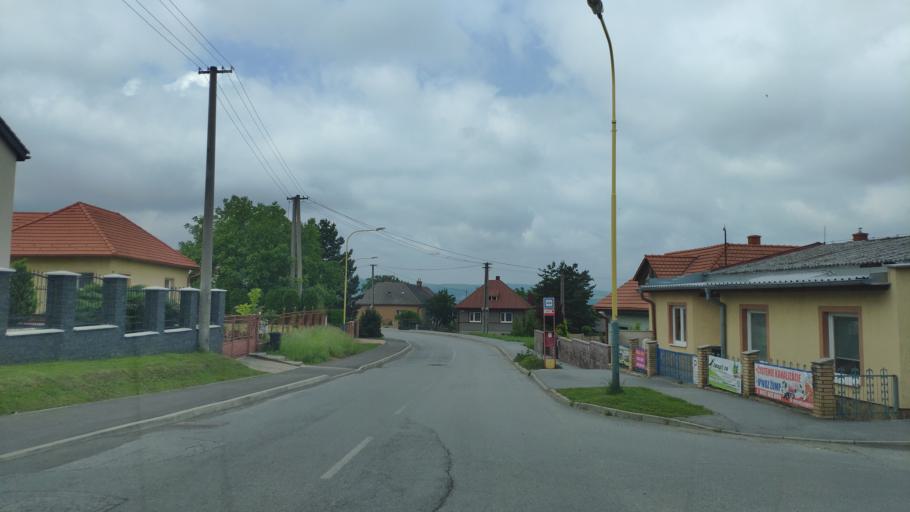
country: SK
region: Presovsky
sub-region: Okres Presov
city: Presov
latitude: 48.9966
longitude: 21.2851
